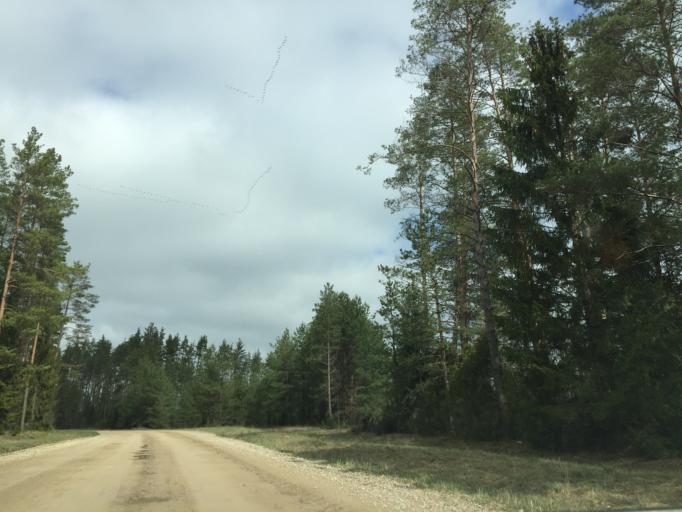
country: EE
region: Valgamaa
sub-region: Valga linn
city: Valga
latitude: 57.6316
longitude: 26.2351
